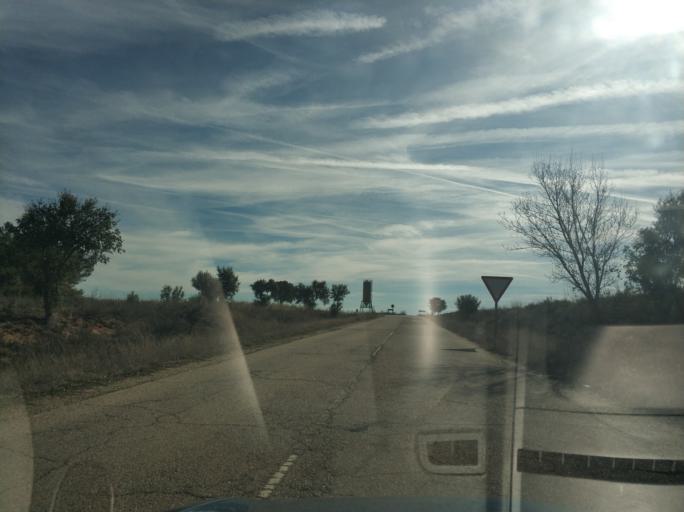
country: ES
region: Castille and Leon
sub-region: Provincia de Zamora
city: Cuelgamures
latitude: 41.2479
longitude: -5.7082
